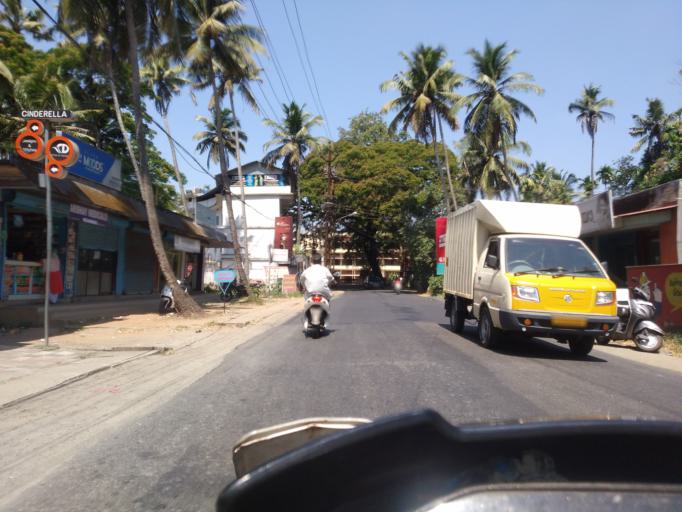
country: IN
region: Kerala
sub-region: Thrissur District
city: Kodungallur
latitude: 10.1779
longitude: 76.2109
